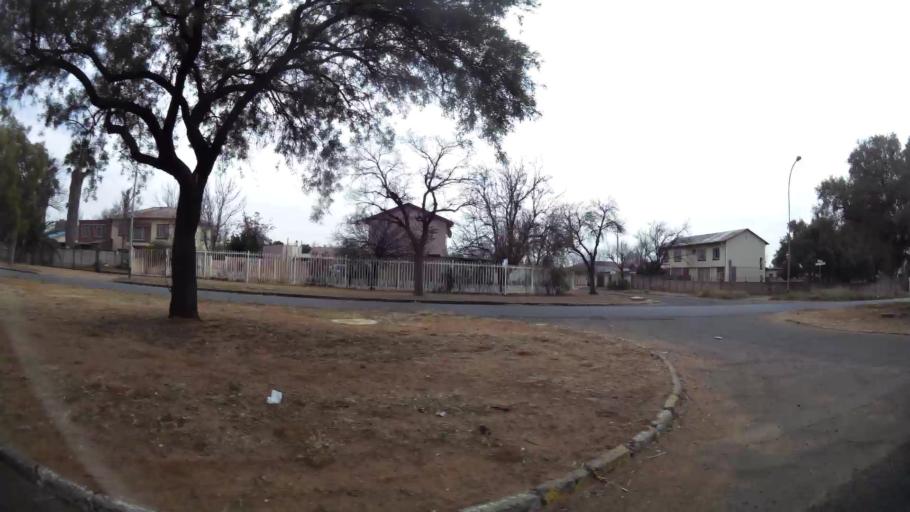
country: ZA
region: Orange Free State
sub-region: Mangaung Metropolitan Municipality
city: Bloemfontein
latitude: -29.1312
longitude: 26.1886
